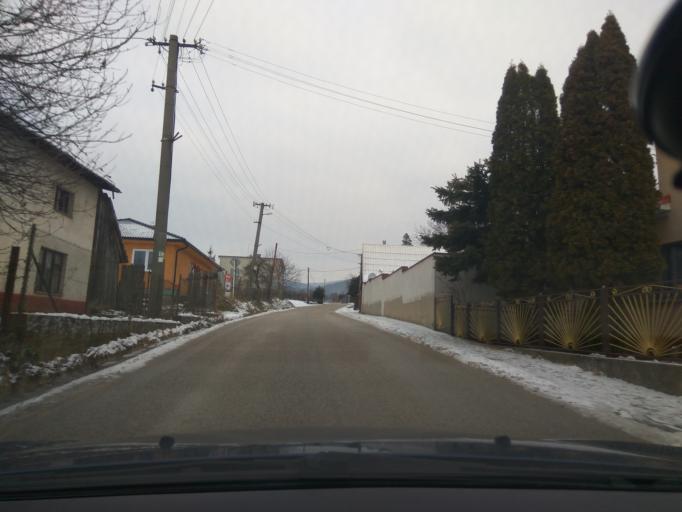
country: SK
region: Nitriansky
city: Stara Tura
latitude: 48.8065
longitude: 17.7109
